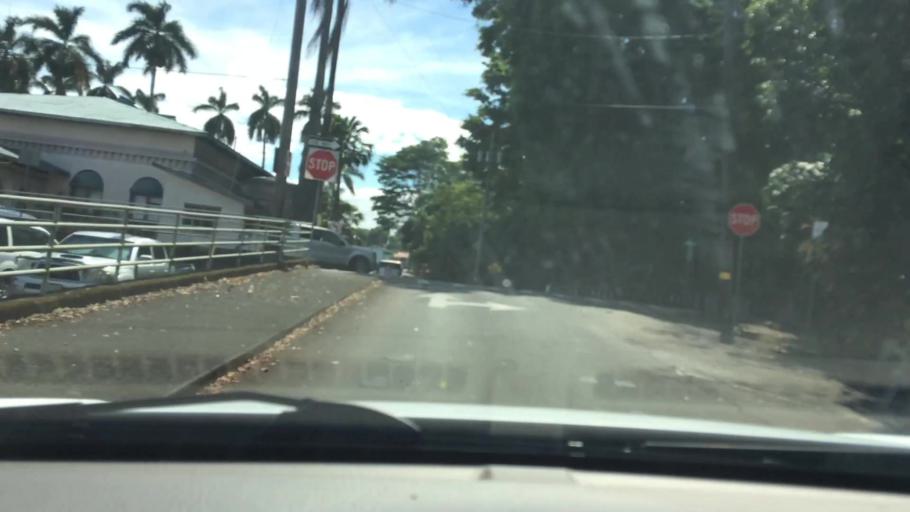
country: US
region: Hawaii
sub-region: Hawaii County
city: Hilo
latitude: 19.7271
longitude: -155.0884
